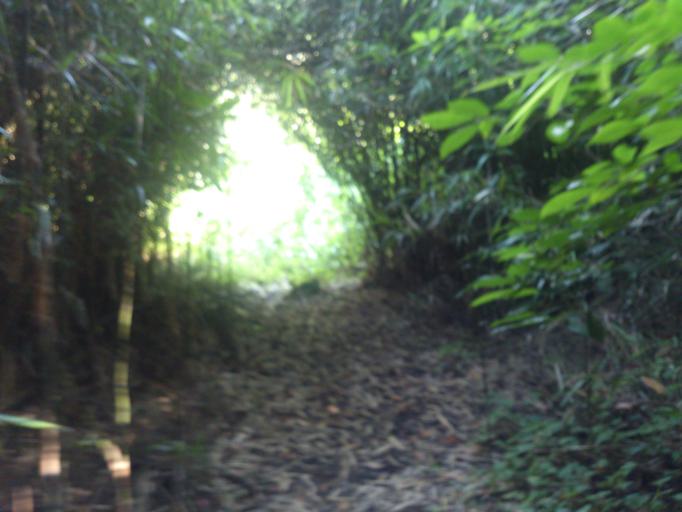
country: JP
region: Chiba
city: Tateyama
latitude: 35.0748
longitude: 139.8342
